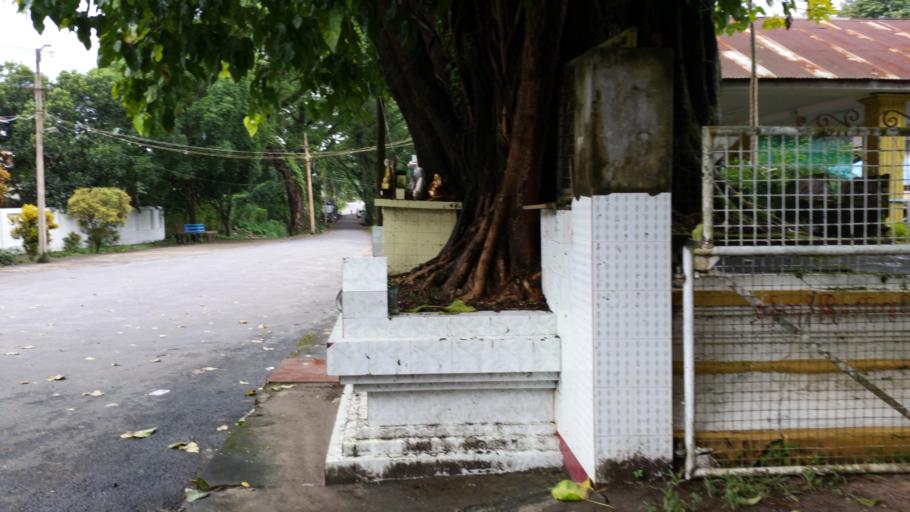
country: MM
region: Mon
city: Mawlamyine
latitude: 16.4890
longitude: 97.6256
